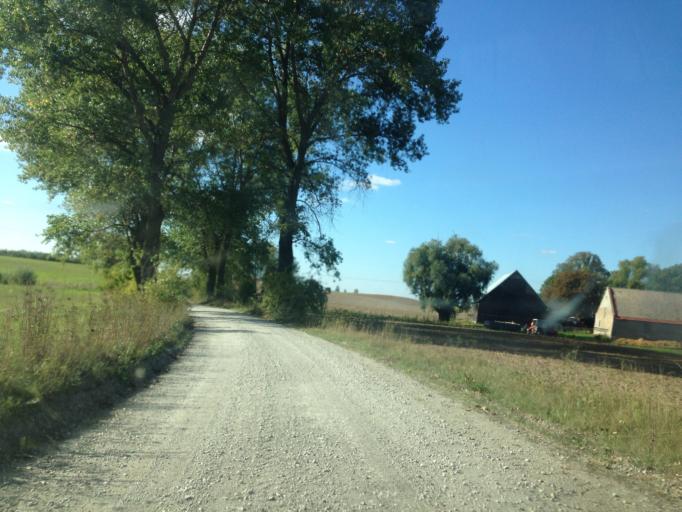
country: PL
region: Kujawsko-Pomorskie
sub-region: Powiat brodnicki
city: Bartniczka
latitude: 53.2236
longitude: 19.5864
